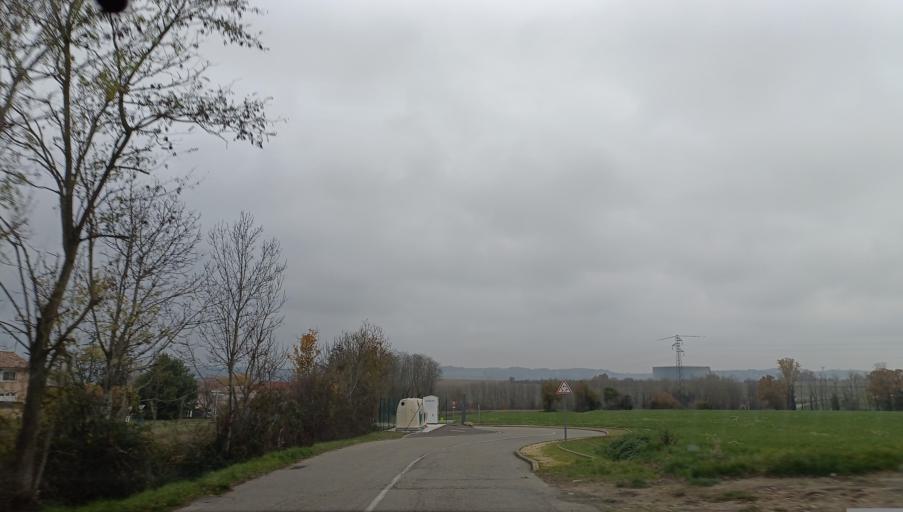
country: FR
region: Rhone-Alpes
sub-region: Departement de l'Isere
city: Serpaize
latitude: 45.5659
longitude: 4.9104
